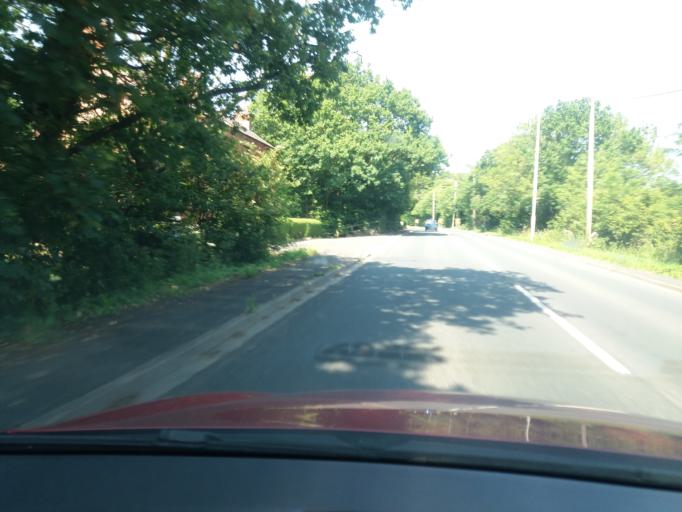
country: GB
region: England
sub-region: Lancashire
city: Coppull
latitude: 53.6374
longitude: -2.6791
